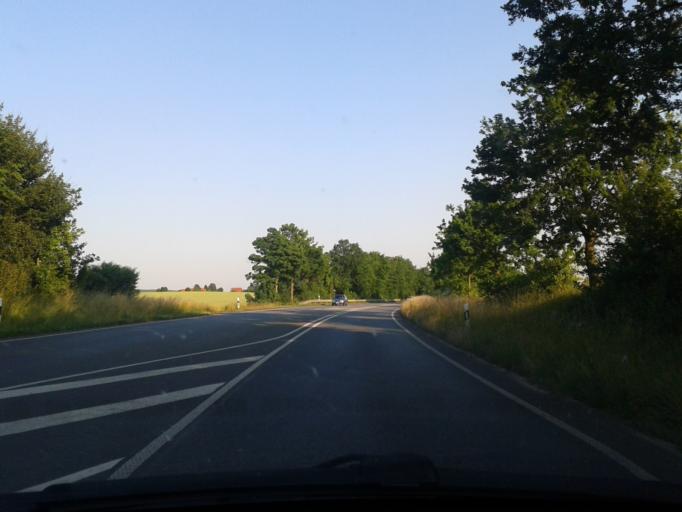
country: DE
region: North Rhine-Westphalia
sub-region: Regierungsbezirk Detmold
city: Detmold
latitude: 51.9426
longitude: 8.9161
